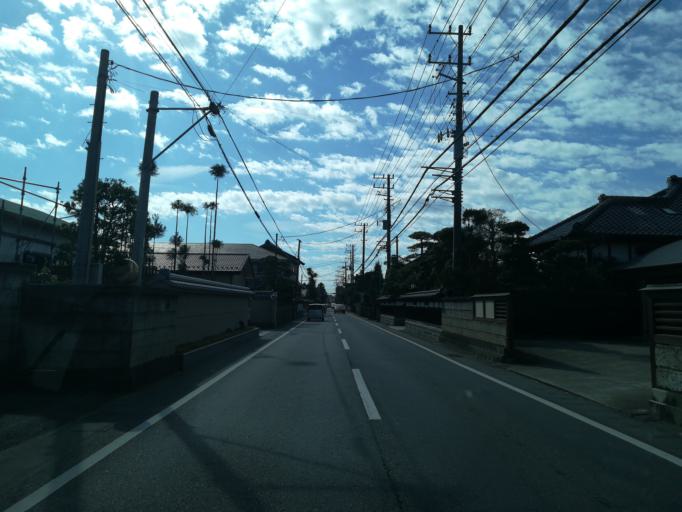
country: JP
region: Ibaraki
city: Naka
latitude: 36.0804
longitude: 140.1007
